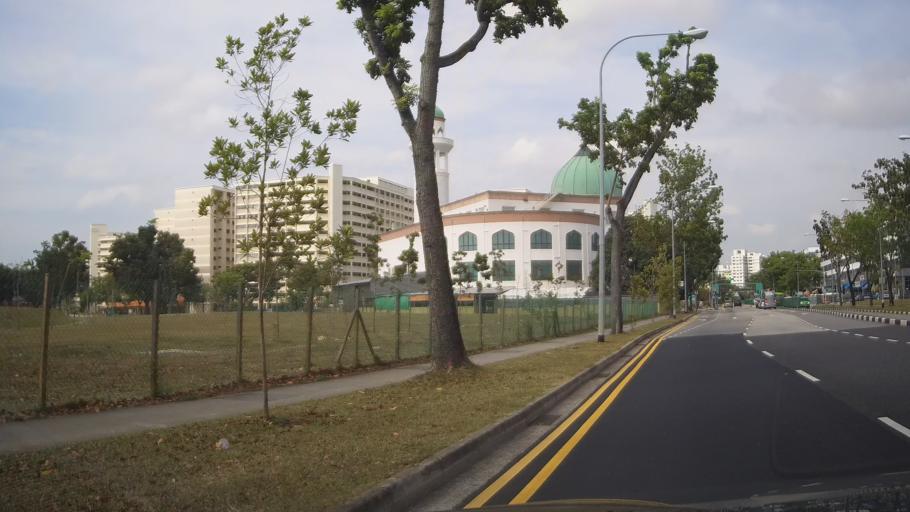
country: SG
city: Singapore
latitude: 1.3374
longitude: 103.9148
